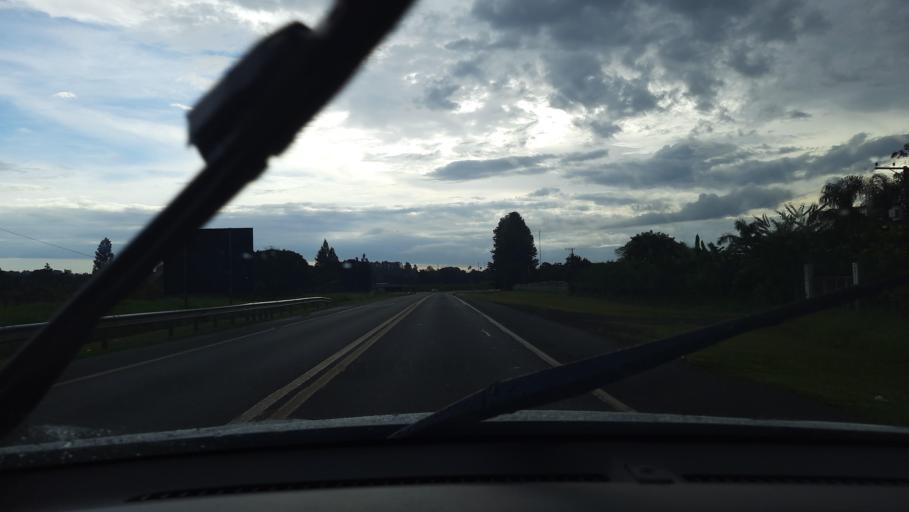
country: BR
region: Sao Paulo
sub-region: Casa Branca
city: Casa Branca
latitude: -21.7725
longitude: -47.0563
